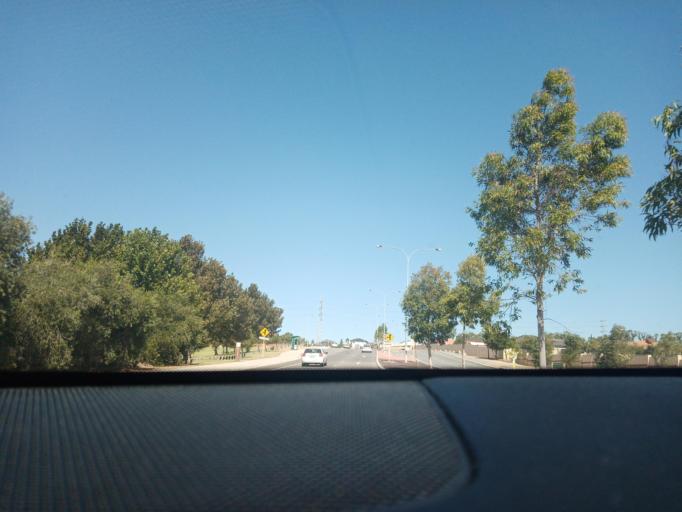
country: AU
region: Western Australia
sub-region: City of Cockburn
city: Beeliar
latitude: -32.1282
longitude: 115.8002
